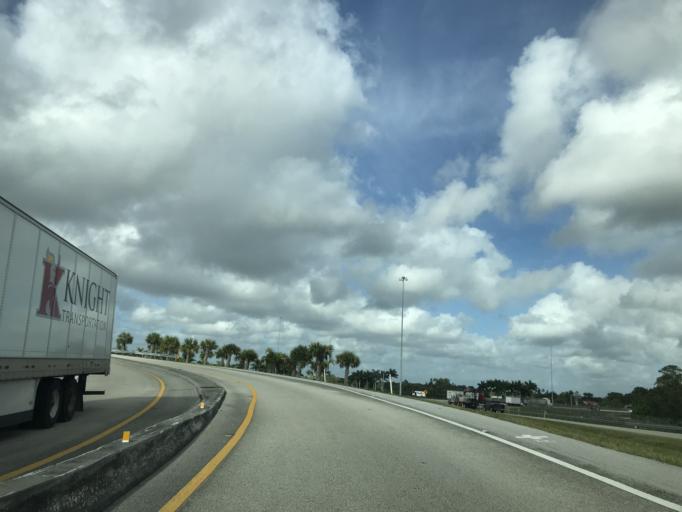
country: US
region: Florida
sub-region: Palm Beach County
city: Boca Del Mar
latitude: 26.3742
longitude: -80.1693
